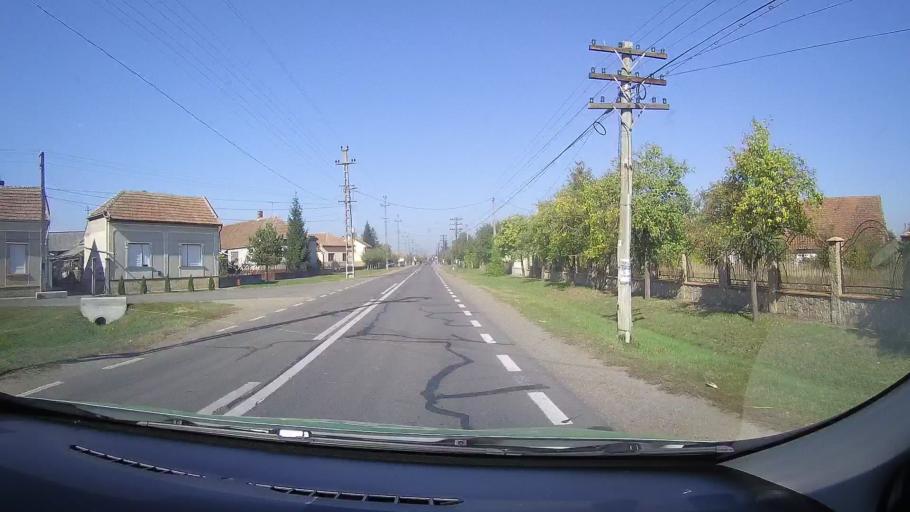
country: RO
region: Satu Mare
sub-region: Comuna Urziceni
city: Urziceni
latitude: 47.7291
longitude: 22.4067
